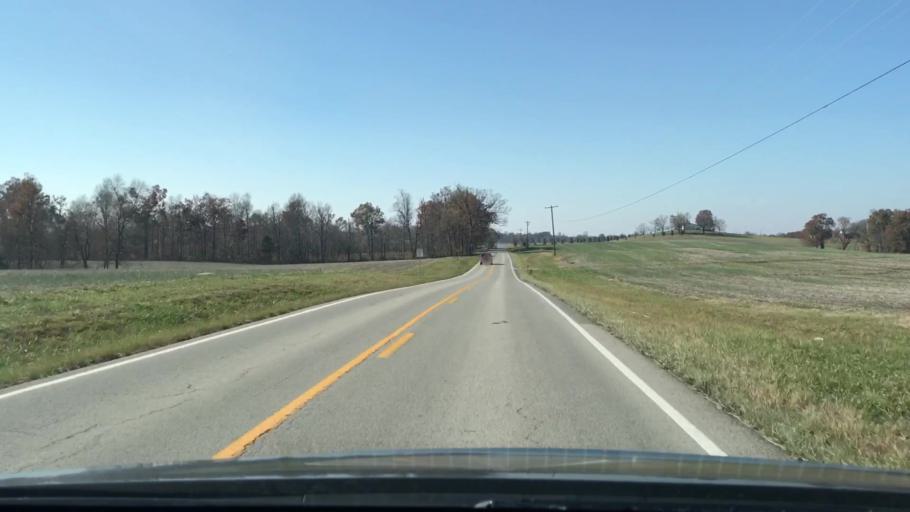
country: US
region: Kentucky
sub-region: Edmonson County
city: Brownsville
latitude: 37.3314
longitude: -86.2528
